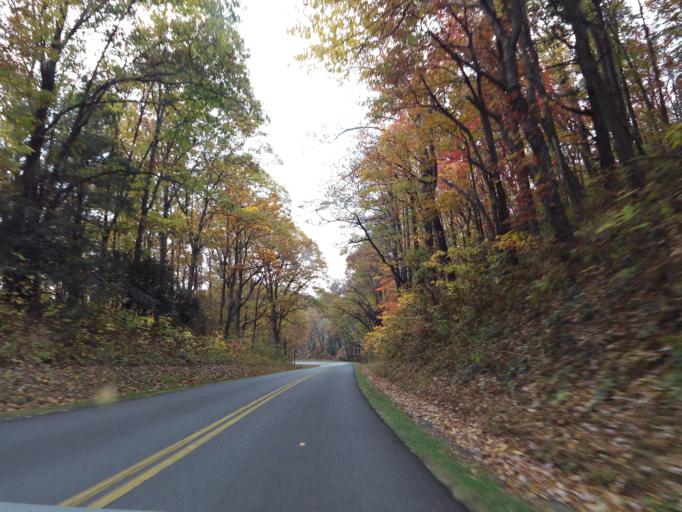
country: US
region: North Carolina
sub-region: Ashe County
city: West Jefferson
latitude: 36.2653
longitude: -81.4316
